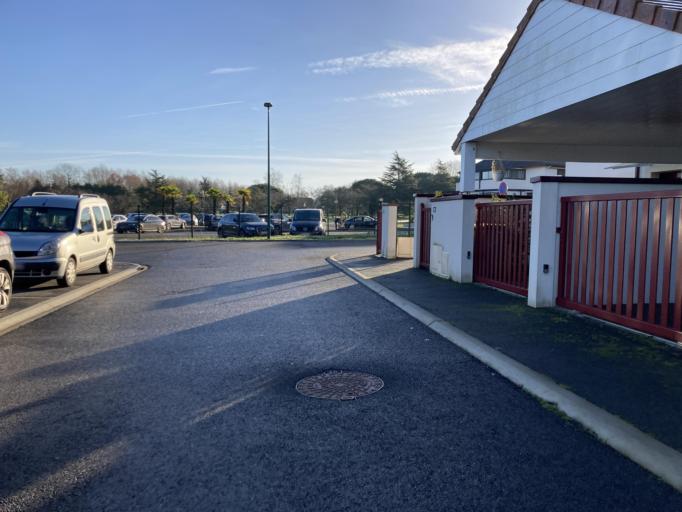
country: FR
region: Aquitaine
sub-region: Departement des Pyrenees-Atlantiques
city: Artiguelouve
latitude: 43.3174
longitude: -0.4586
